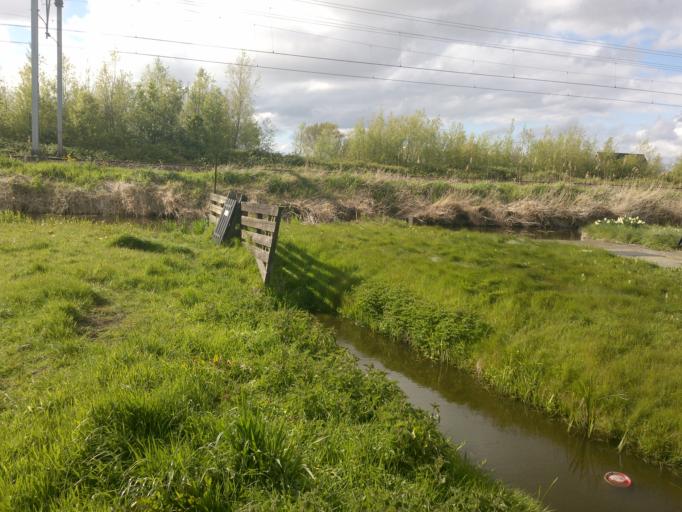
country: NL
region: South Holland
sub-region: Gemeente Lisse
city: Lisse
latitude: 52.2643
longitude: 4.5254
